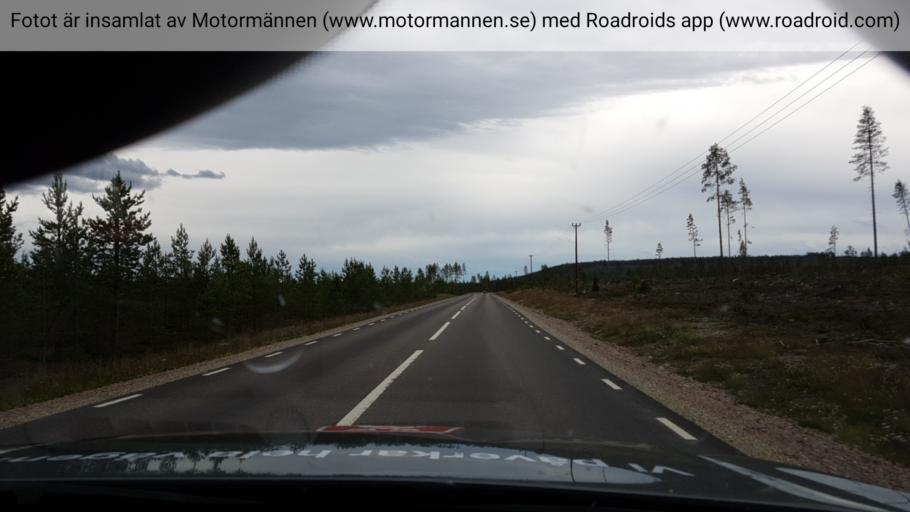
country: SE
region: Jaemtland
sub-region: Bergs Kommun
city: Hoverberg
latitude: 62.4745
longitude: 14.2672
